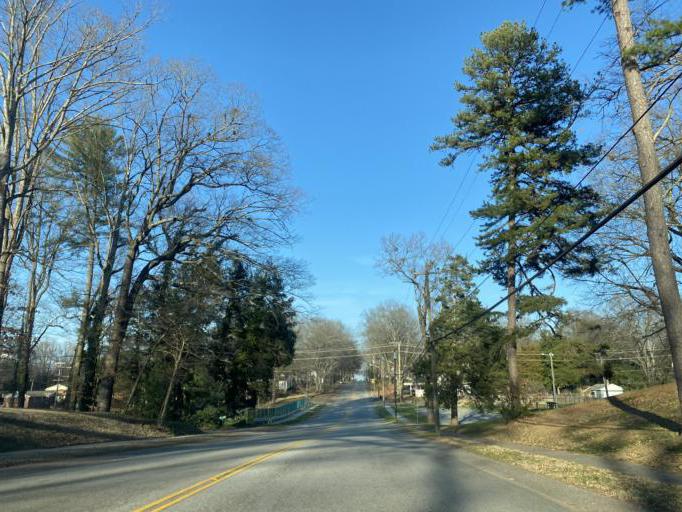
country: US
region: South Carolina
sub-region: Cherokee County
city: Gaffney
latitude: 35.0650
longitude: -81.6562
